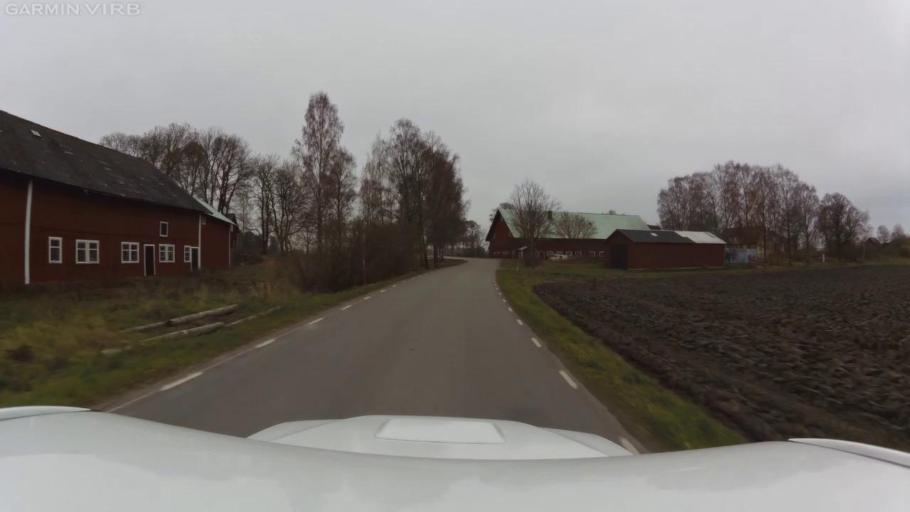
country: SE
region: OEstergoetland
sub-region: Linkopings Kommun
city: Vikingstad
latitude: 58.3213
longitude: 15.3764
